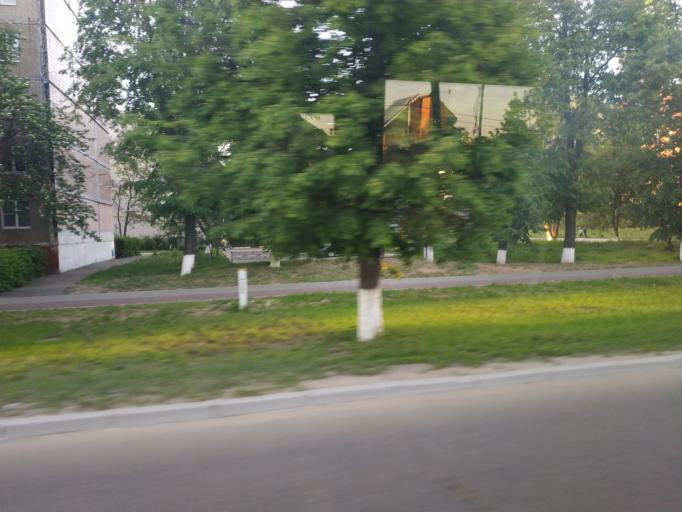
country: RU
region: Moskovskaya
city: Domodedovo
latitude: 55.4436
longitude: 37.7455
